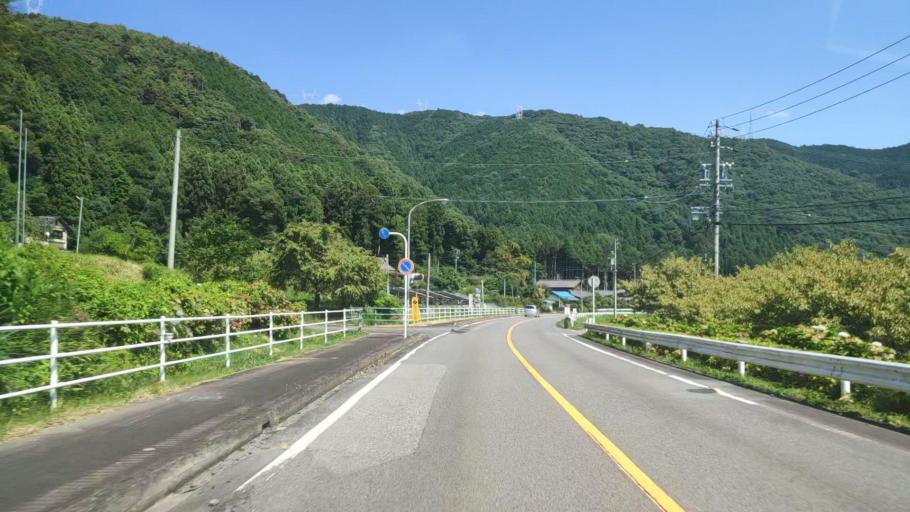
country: JP
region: Gifu
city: Godo
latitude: 35.5572
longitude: 136.6436
